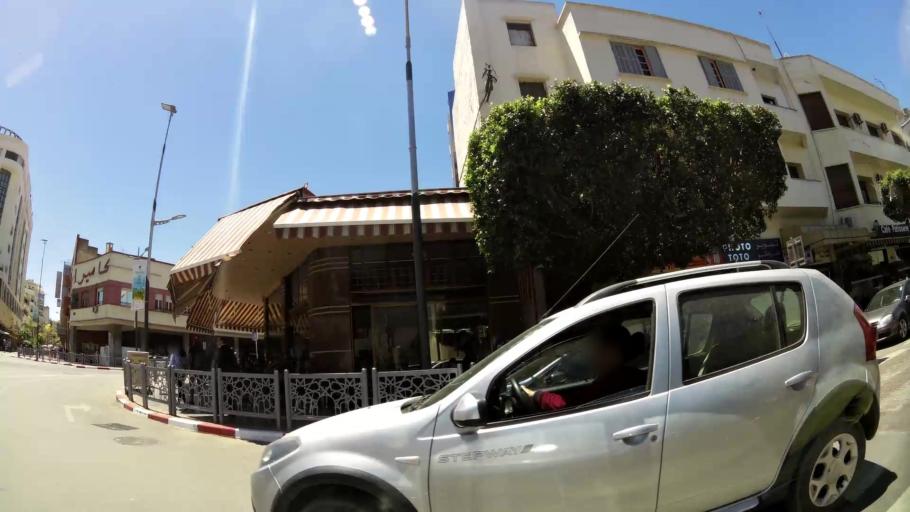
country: MA
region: Meknes-Tafilalet
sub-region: Meknes
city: Meknes
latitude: 33.9006
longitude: -5.5492
